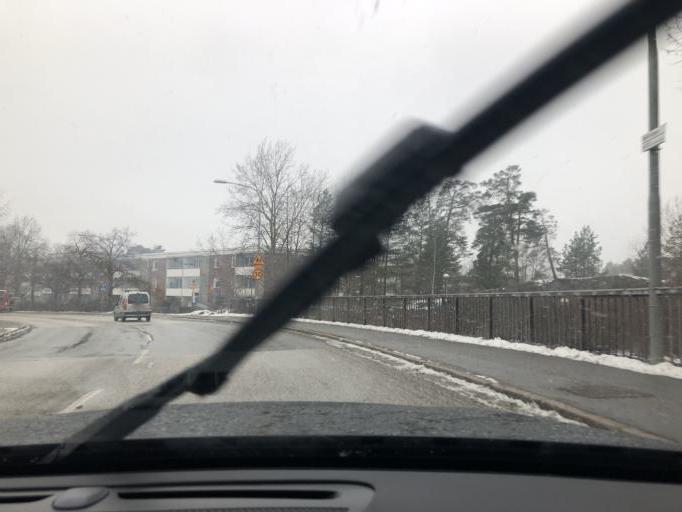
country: SE
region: Stockholm
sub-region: Nacka Kommun
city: Nacka
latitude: 59.2812
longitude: 18.1293
